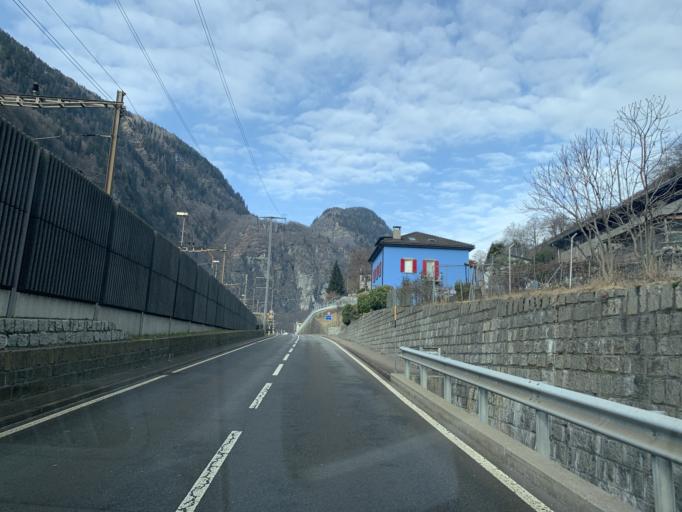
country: CH
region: Ticino
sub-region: Leventina District
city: Faido
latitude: 46.4386
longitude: 8.8447
